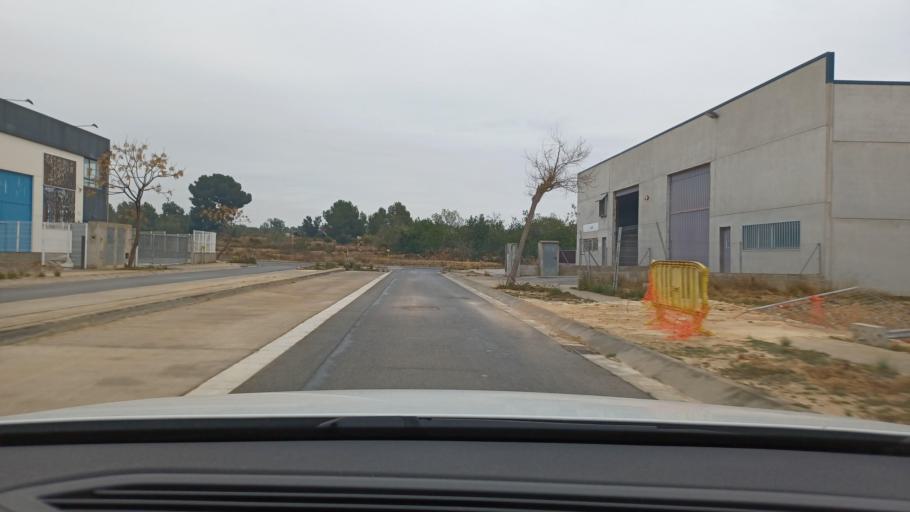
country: ES
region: Catalonia
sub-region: Provincia de Tarragona
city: Amposta
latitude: 40.7678
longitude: 0.5959
